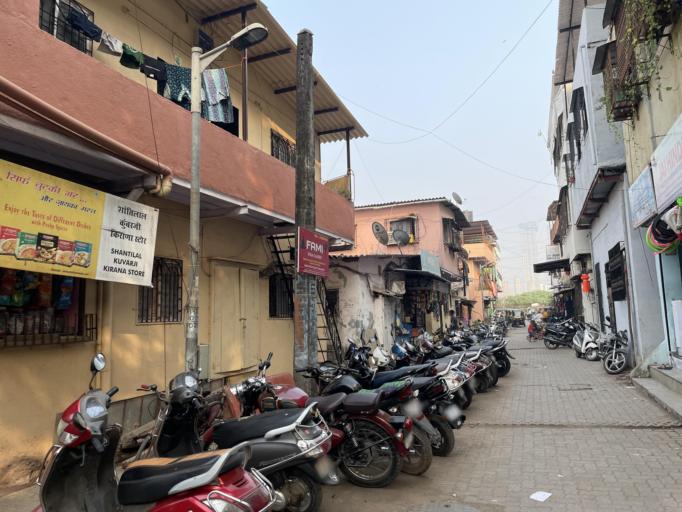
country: IN
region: Maharashtra
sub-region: Mumbai Suburban
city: Borivli
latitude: 19.1930
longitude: 72.8213
